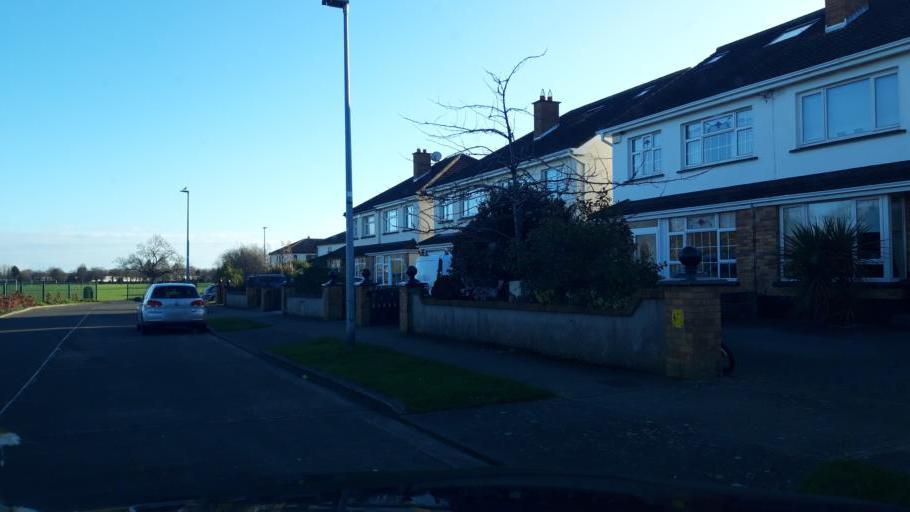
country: IE
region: Leinster
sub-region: Fingal County
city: Swords
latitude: 53.4556
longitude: -6.2484
